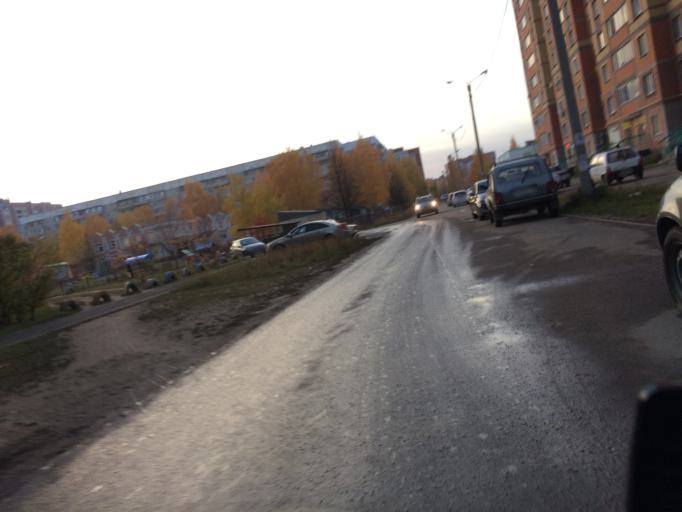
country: RU
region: Mariy-El
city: Yoshkar-Ola
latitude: 56.6314
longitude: 47.9275
